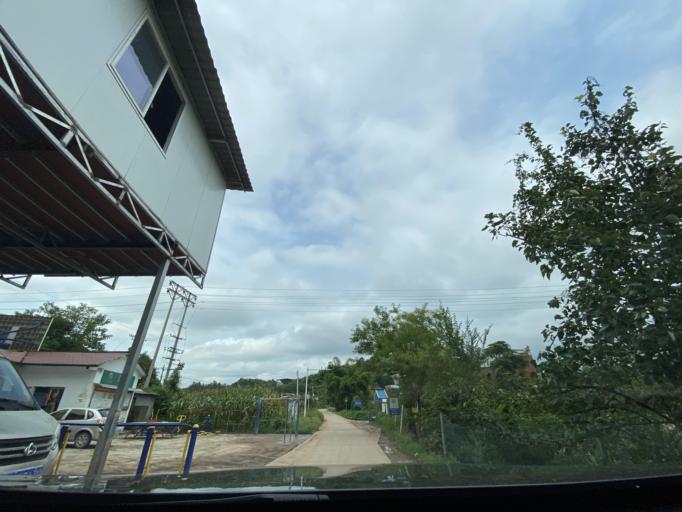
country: CN
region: Sichuan
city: Jiancheng
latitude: 30.4009
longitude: 104.5678
